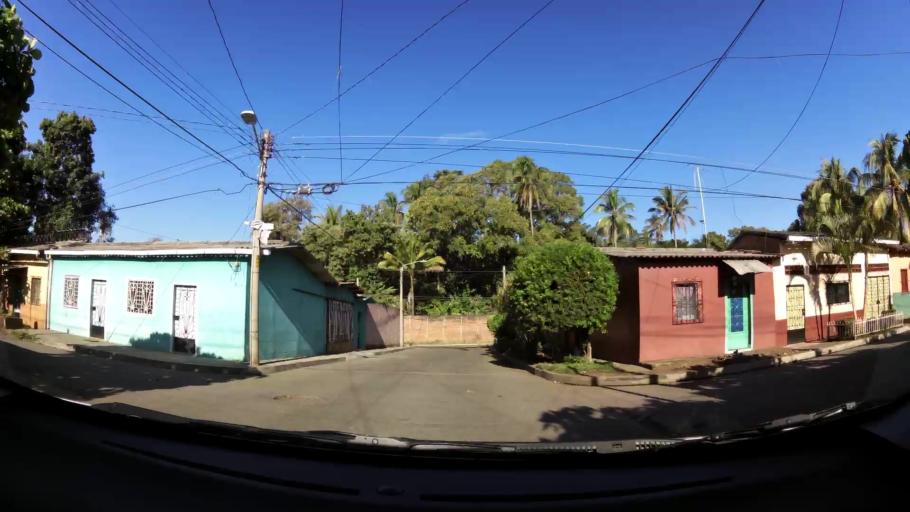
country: SV
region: Sonsonate
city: Sonsonate
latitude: 13.7132
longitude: -89.7216
